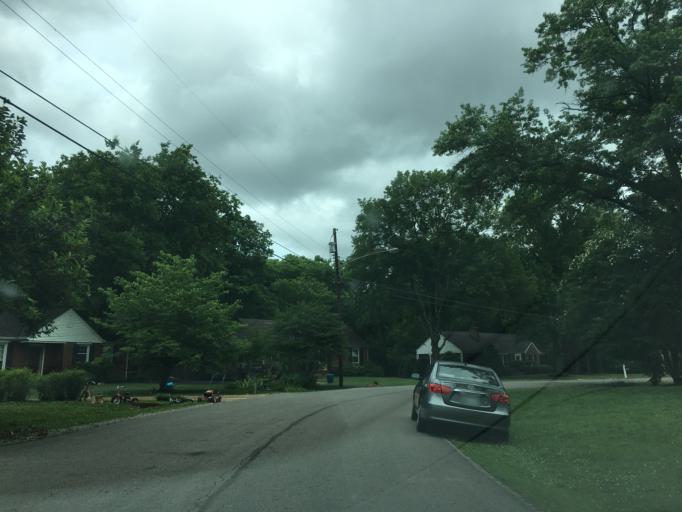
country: US
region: Tennessee
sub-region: Davidson County
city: Oak Hill
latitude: 36.1120
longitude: -86.7788
